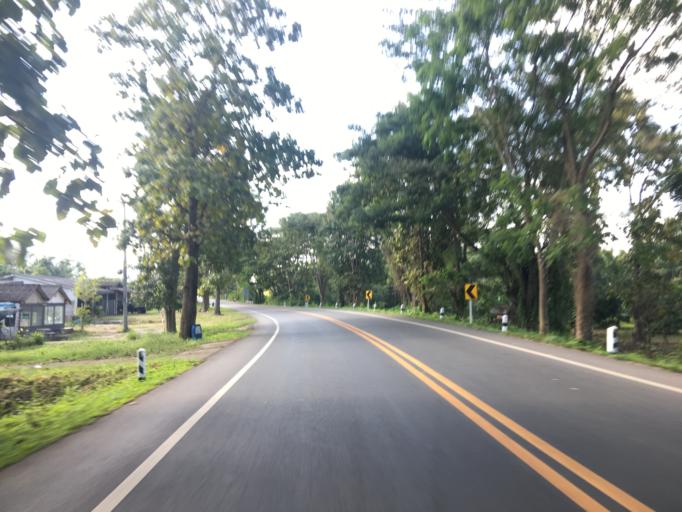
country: TH
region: Phayao
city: Chun
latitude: 19.3488
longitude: 100.1122
